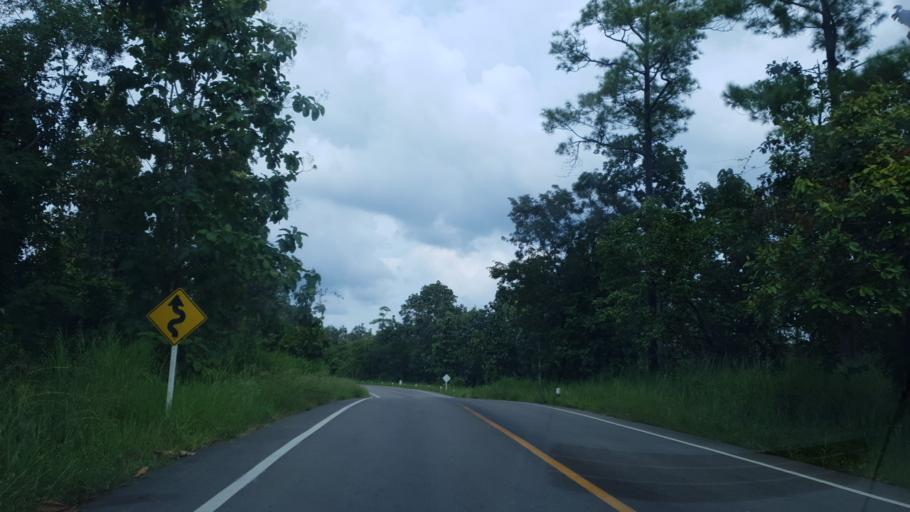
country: TH
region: Mae Hong Son
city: Khun Yuam
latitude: 18.7532
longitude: 97.9272
